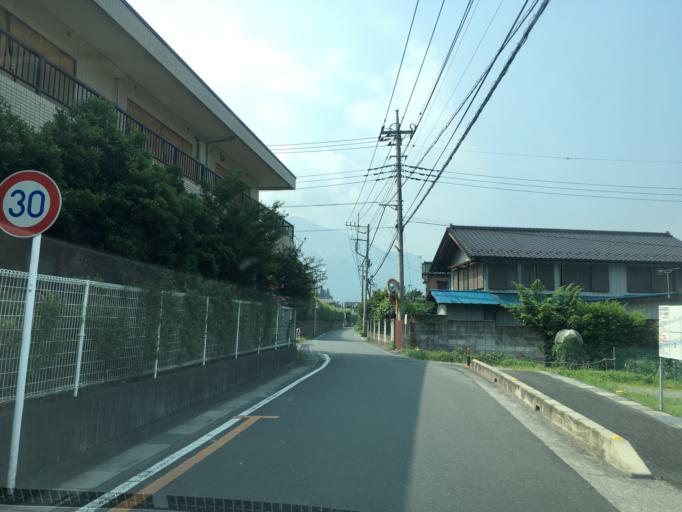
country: JP
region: Saitama
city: Chichibu
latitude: 36.0055
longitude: 139.1100
